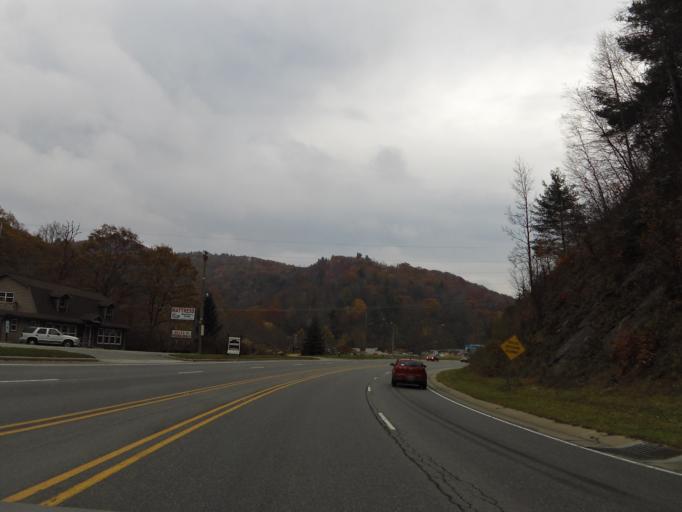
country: US
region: North Carolina
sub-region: Watauga County
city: Boone
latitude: 36.1809
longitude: -81.6478
